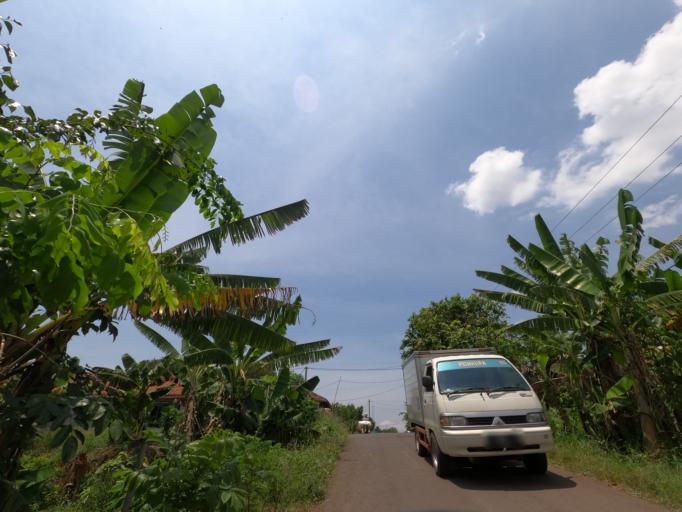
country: ID
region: West Java
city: Pamanukan
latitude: -6.5163
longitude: 107.7726
